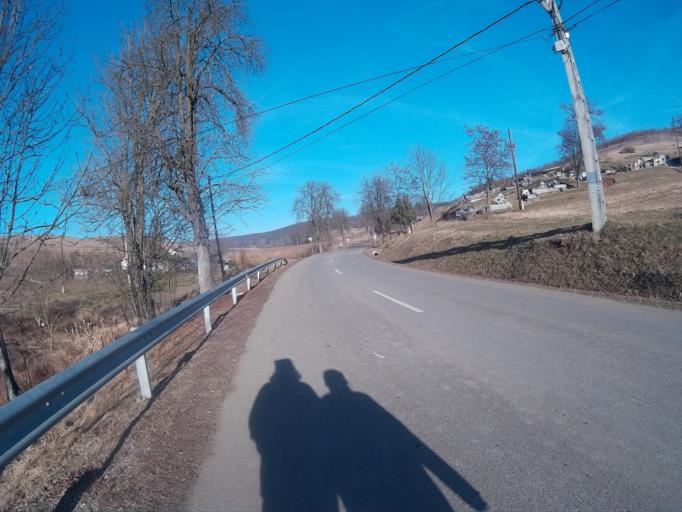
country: HU
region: Borsod-Abauj-Zemplen
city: Putnok
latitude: 48.3892
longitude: 20.4881
